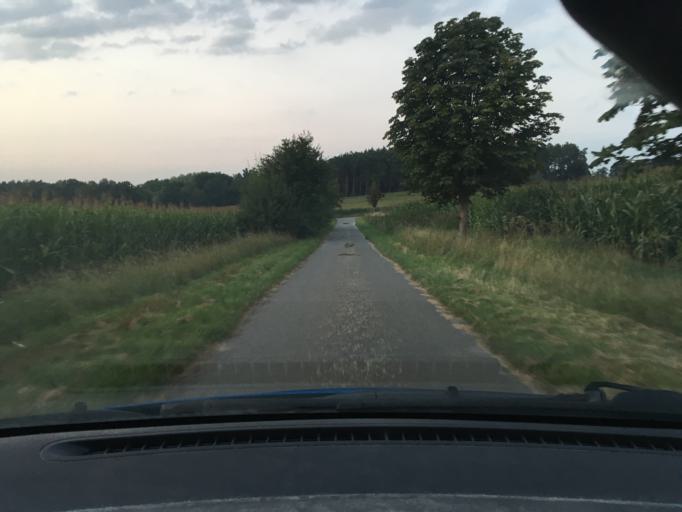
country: DE
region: Lower Saxony
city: Altenmedingen
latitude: 53.1840
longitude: 10.6230
